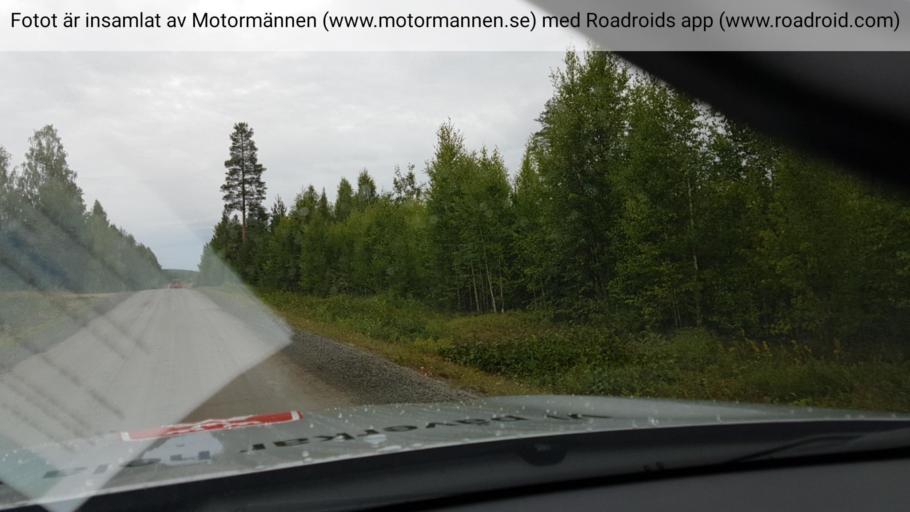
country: SE
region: Norrbotten
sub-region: Alvsbyns Kommun
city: AElvsbyn
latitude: 65.9531
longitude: 21.2314
